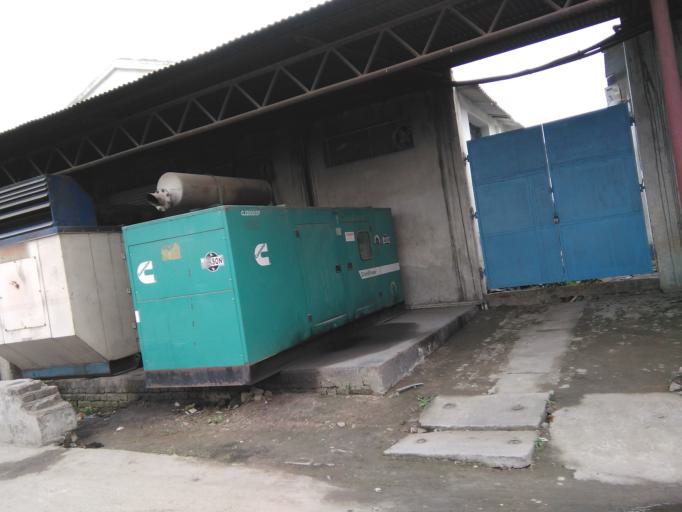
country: IN
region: Bihar
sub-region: Muzaffarpur
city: Muzaffarpur
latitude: 26.1006
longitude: 85.4095
